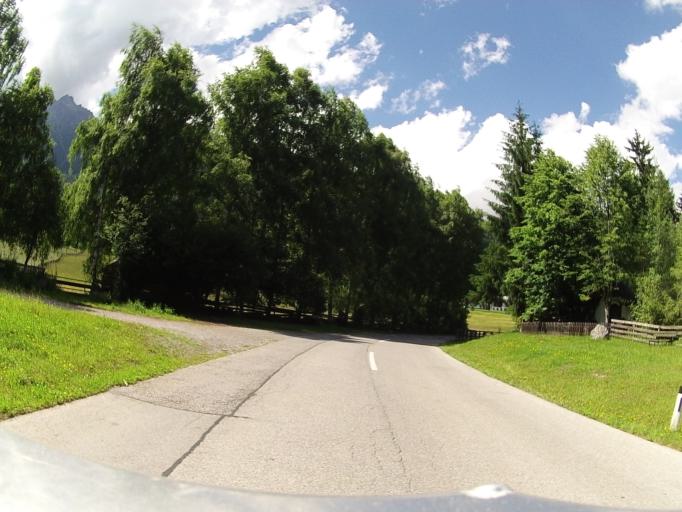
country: AT
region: Tyrol
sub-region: Politischer Bezirk Imst
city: Imst
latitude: 47.2588
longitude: 10.7387
